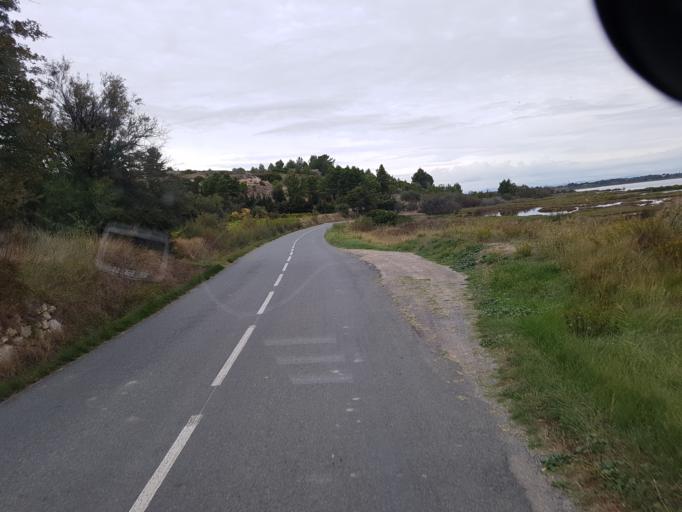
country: FR
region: Languedoc-Roussillon
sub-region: Departement de l'Aude
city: Peyriac-de-Mer
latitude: 43.1300
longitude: 2.9860
